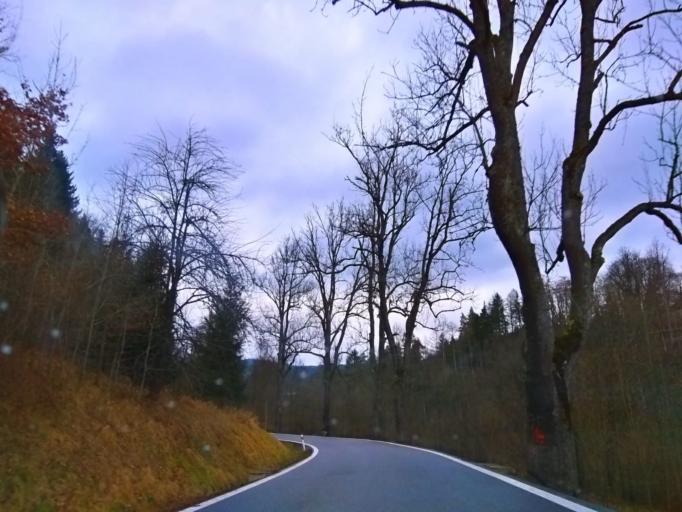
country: CZ
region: Jihocesky
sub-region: Okres Cesky Krumlov
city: Vyssi Brod
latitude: 48.6564
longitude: 14.3632
